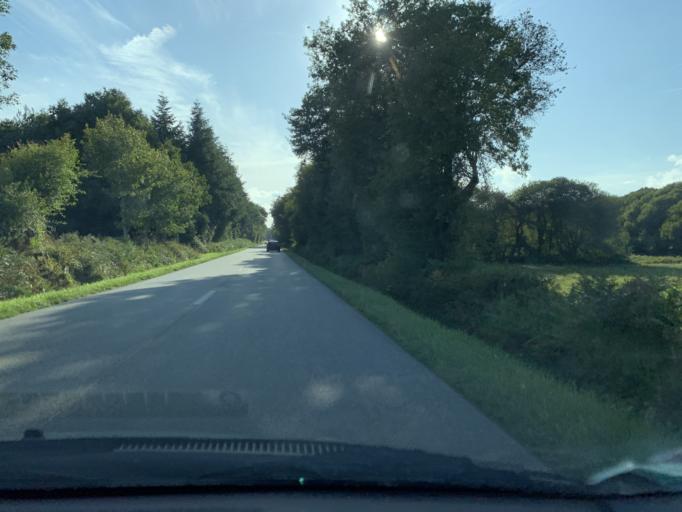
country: FR
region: Brittany
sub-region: Departement du Morbihan
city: Surzur
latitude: 47.5664
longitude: -2.6732
